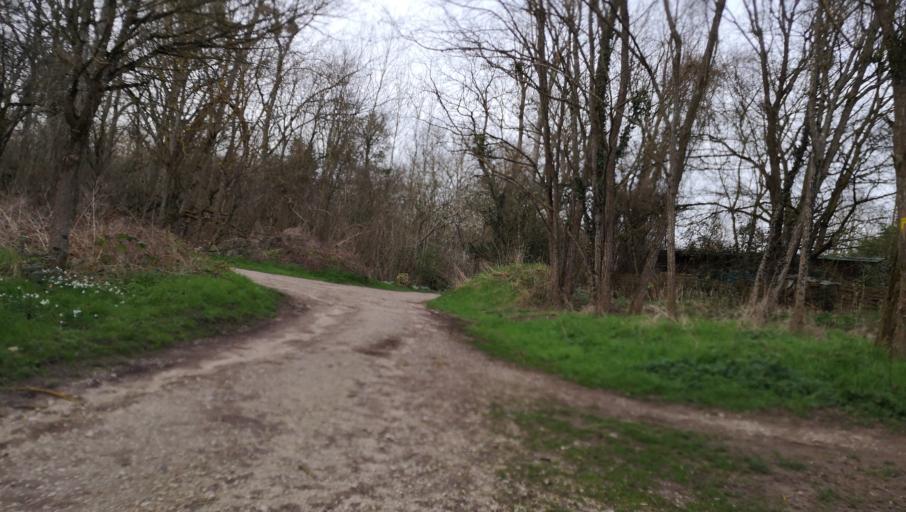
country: FR
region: Centre
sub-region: Departement du Loiret
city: La Chapelle-Saint-Mesmin
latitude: 47.8793
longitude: 1.8306
